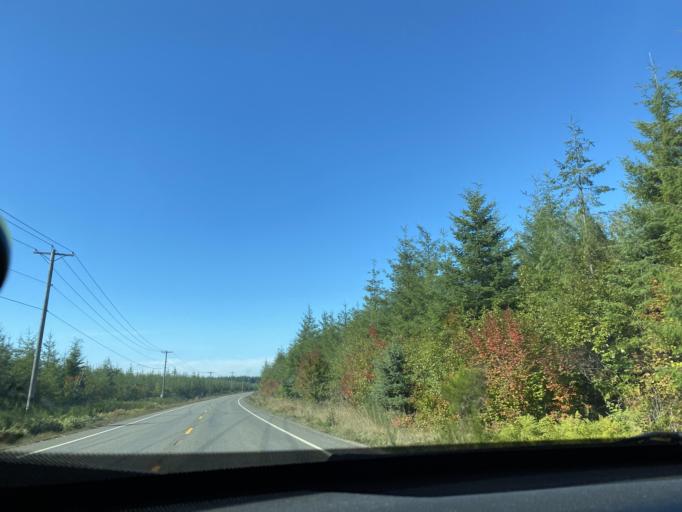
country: US
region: Washington
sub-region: Clallam County
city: Forks
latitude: 47.9646
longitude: -124.4166
